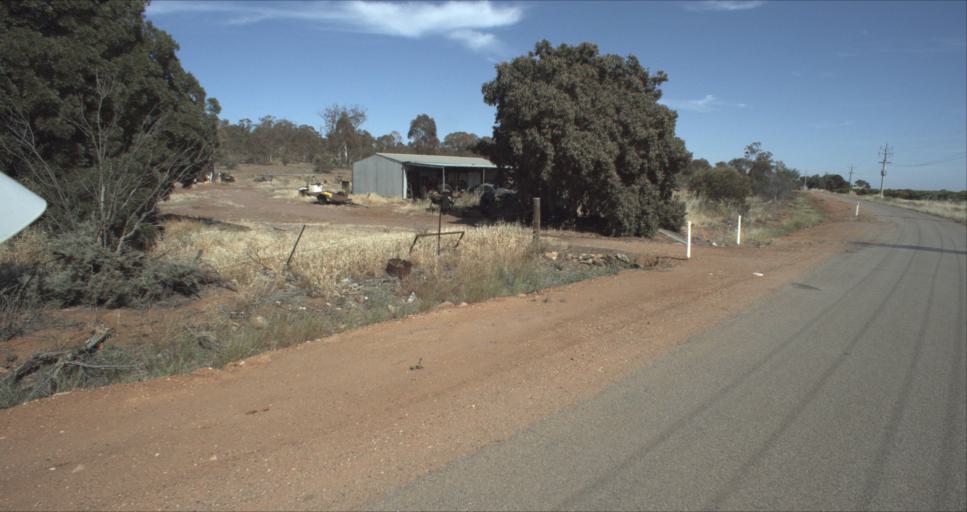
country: AU
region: New South Wales
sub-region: Leeton
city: Leeton
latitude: -34.5796
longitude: 146.4874
